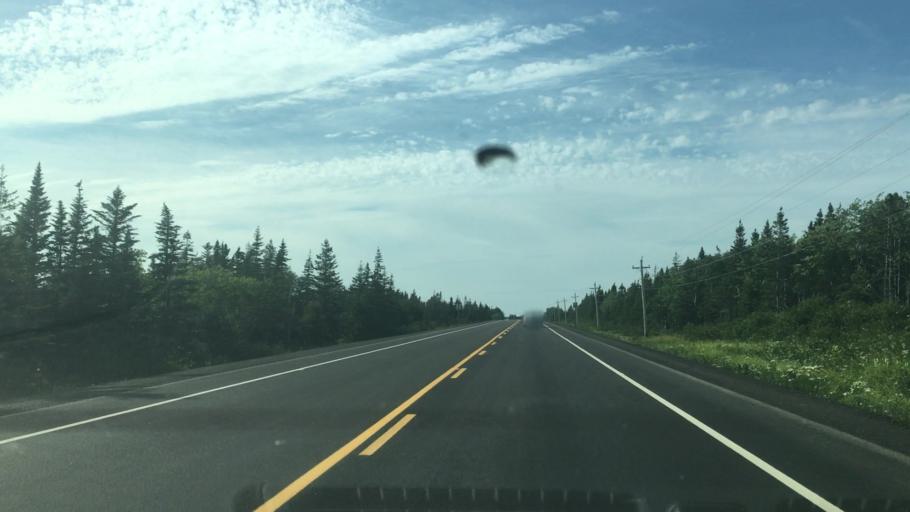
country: CA
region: Nova Scotia
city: Sydney Mines
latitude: 46.8456
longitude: -60.4096
